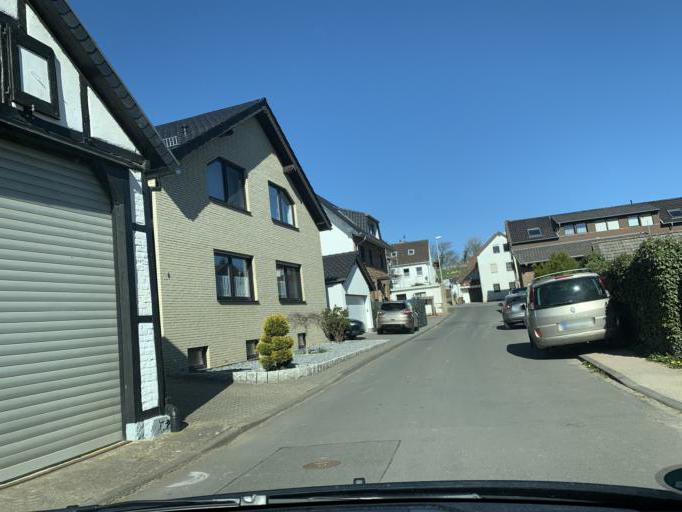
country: DE
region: North Rhine-Westphalia
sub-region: Regierungsbezirk Koln
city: Nideggen
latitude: 50.7143
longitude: 6.4974
